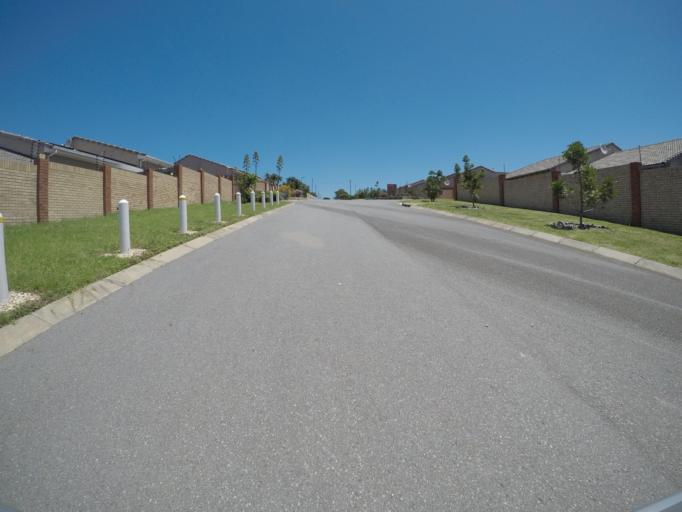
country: ZA
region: Eastern Cape
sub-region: Buffalo City Metropolitan Municipality
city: East London
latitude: -32.9546
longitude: 27.9419
